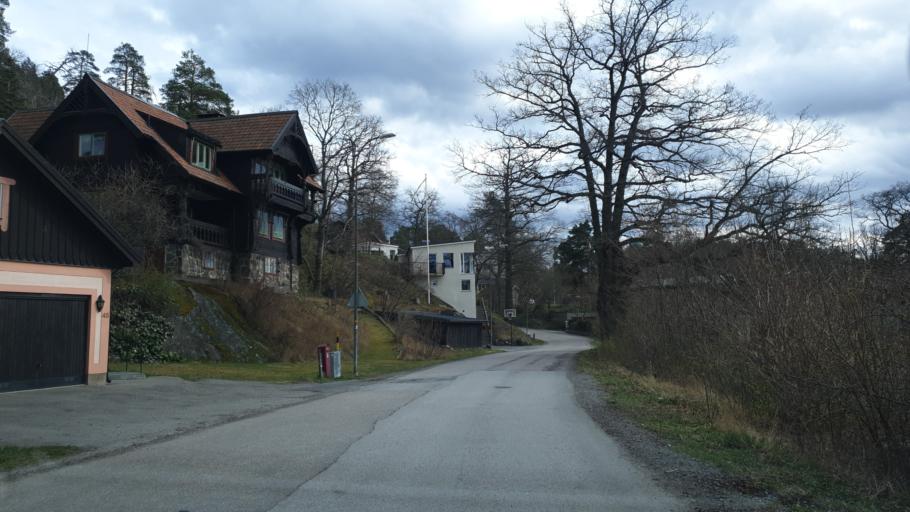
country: SE
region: Stockholm
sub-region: Nacka Kommun
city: Saltsjobaden
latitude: 59.2774
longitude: 18.3019
